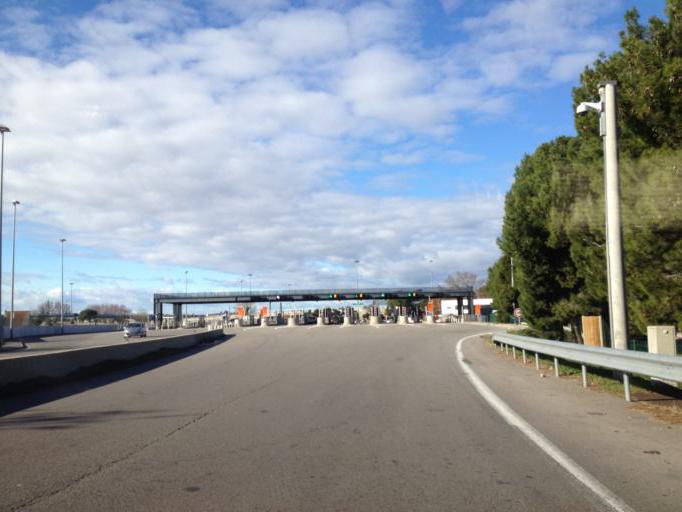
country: FR
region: Provence-Alpes-Cote d'Azur
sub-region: Departement du Vaucluse
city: Vedene
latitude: 43.9815
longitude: 4.8899
